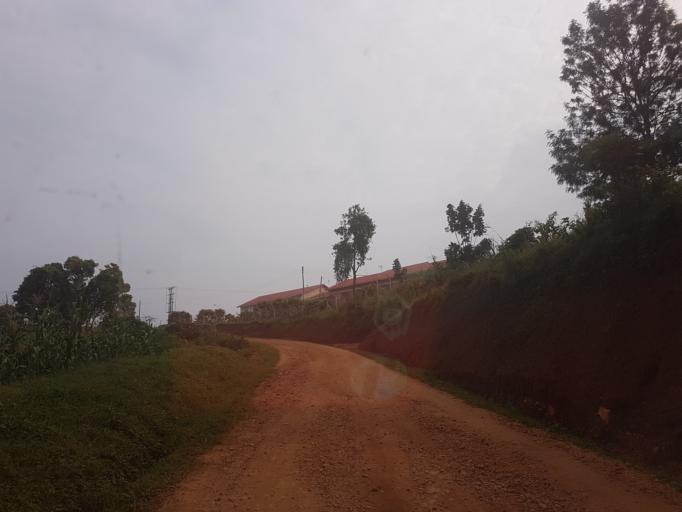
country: UG
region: Western Region
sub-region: Kanungu District
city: Kanungu
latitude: -0.8955
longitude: 29.7775
